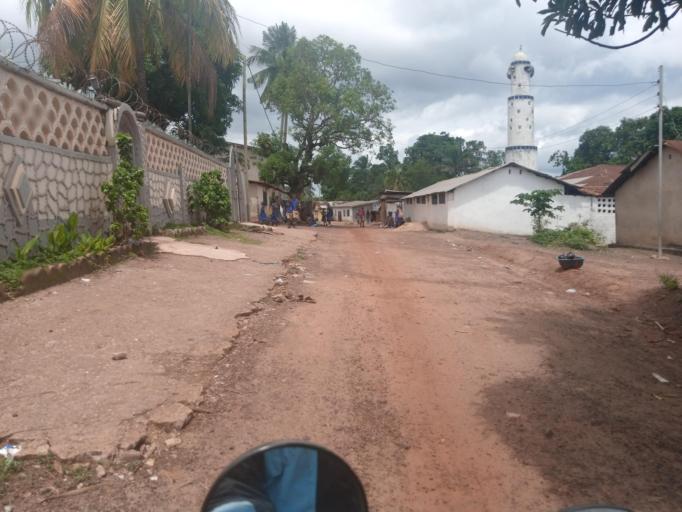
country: SL
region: Southern Province
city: Bo
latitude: 7.9569
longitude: -11.7397
